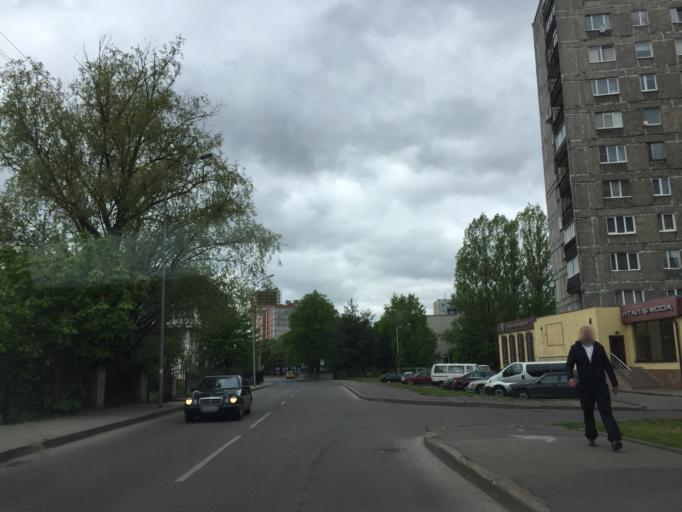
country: RU
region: Kaliningrad
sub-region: Gorod Kaliningrad
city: Kaliningrad
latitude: 54.7071
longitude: 20.4973
